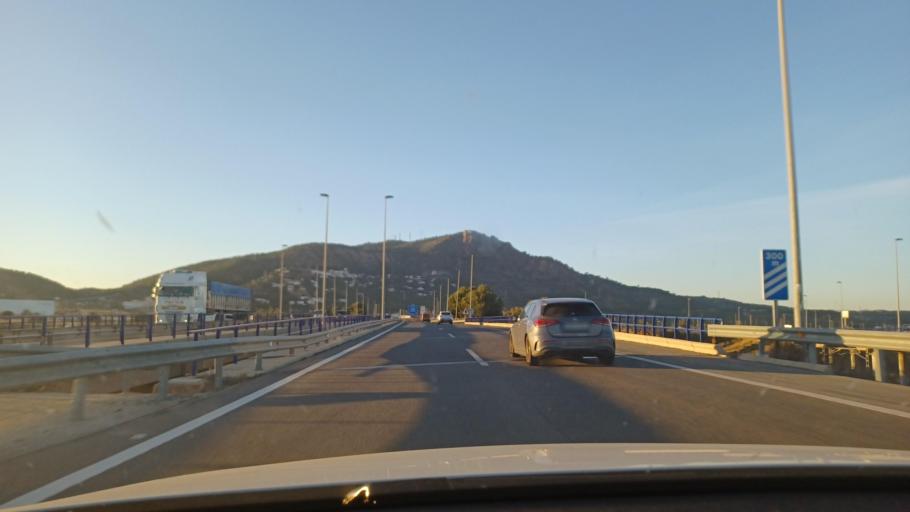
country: ES
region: Valencia
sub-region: Provincia de Valencia
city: Pucol
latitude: 39.6268
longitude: -0.2974
